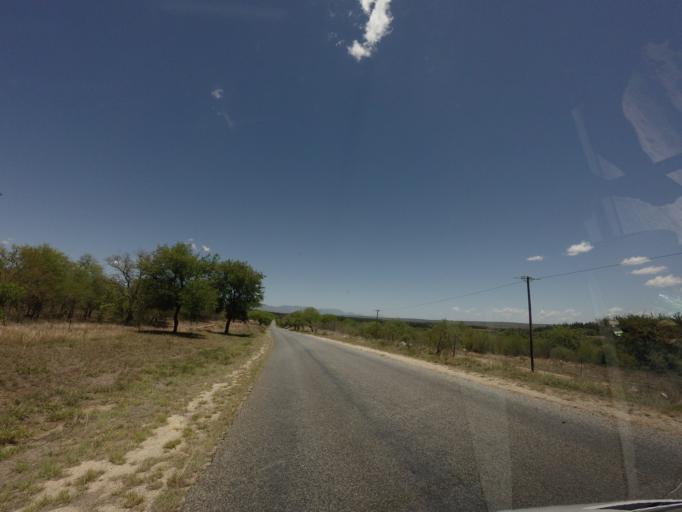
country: ZA
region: Limpopo
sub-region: Mopani District Municipality
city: Hoedspruit
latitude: -24.3710
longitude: 30.7278
